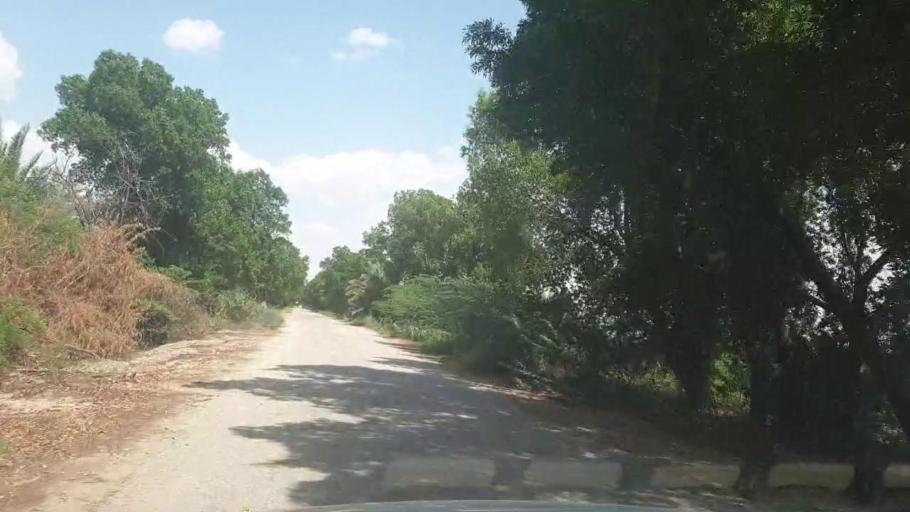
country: PK
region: Sindh
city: Kot Diji
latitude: 27.2200
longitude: 69.0453
